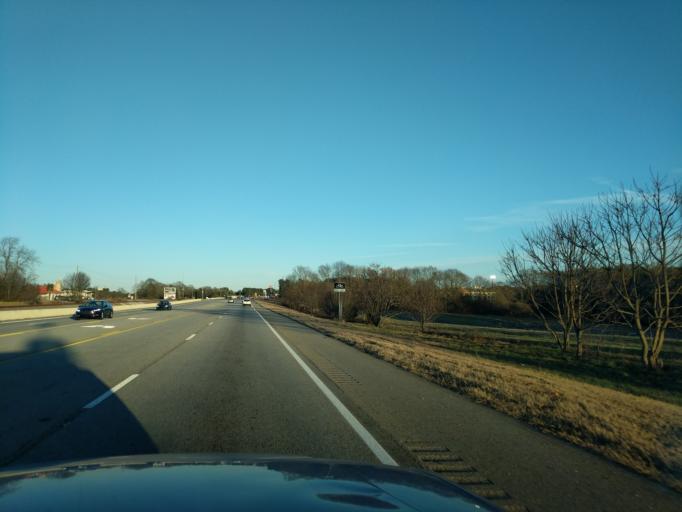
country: US
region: Georgia
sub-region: Franklin County
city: Lavonia
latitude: 34.4478
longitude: -83.1343
